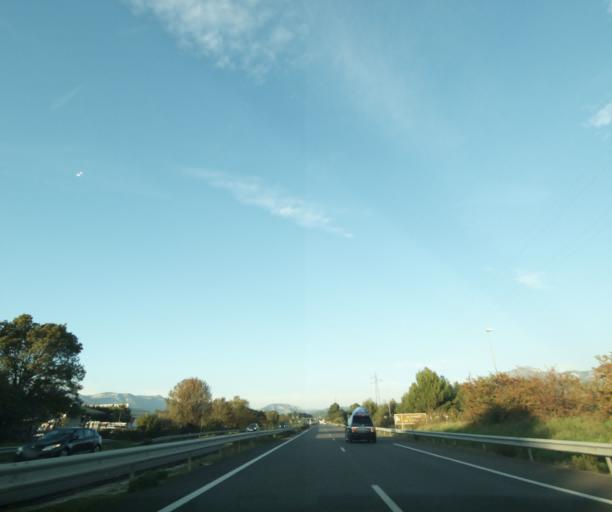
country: FR
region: Provence-Alpes-Cote d'Azur
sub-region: Departement des Bouches-du-Rhone
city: Aubagne
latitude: 43.2912
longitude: 5.5872
